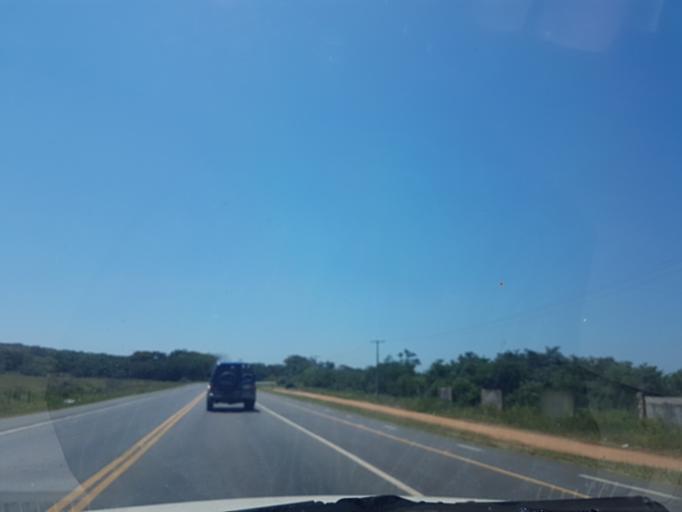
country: PY
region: Cordillera
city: San Bernardino
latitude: -25.2701
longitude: -57.3207
